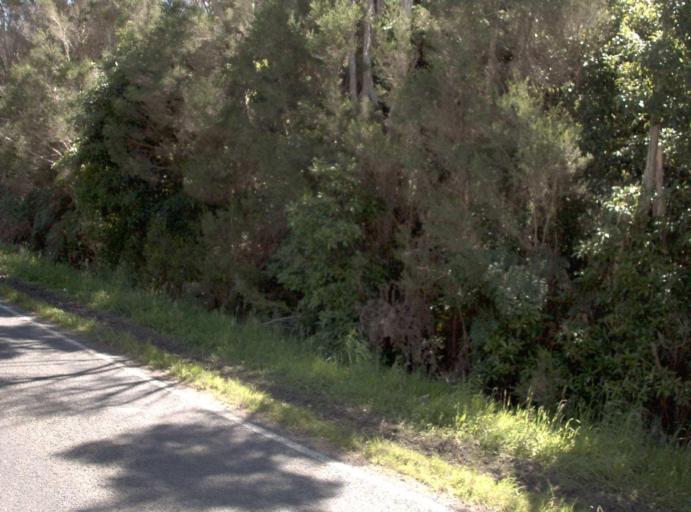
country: AU
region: Victoria
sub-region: Latrobe
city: Morwell
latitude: -38.6960
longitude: 146.1794
